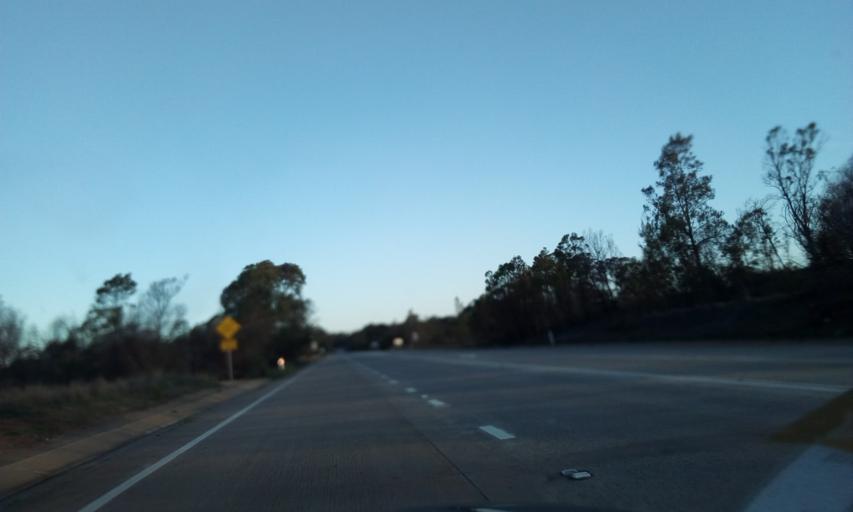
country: AU
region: New South Wales
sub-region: Wollondilly
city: Douglas Park
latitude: -34.2424
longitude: 150.6968
